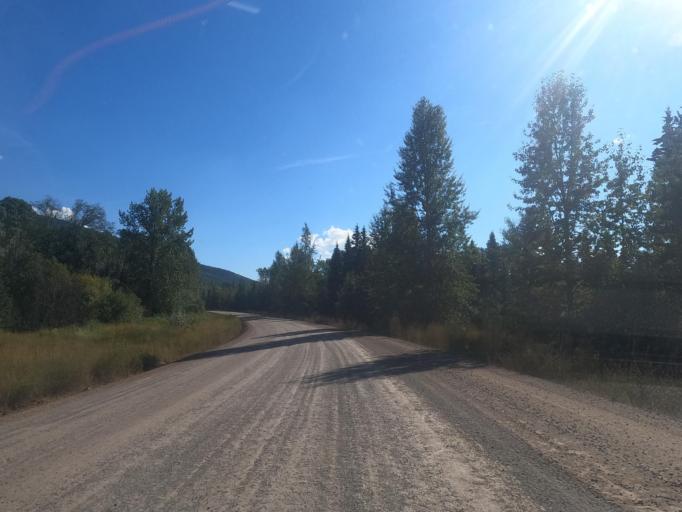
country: CA
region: British Columbia
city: Houston
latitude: 54.2889
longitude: -126.8504
